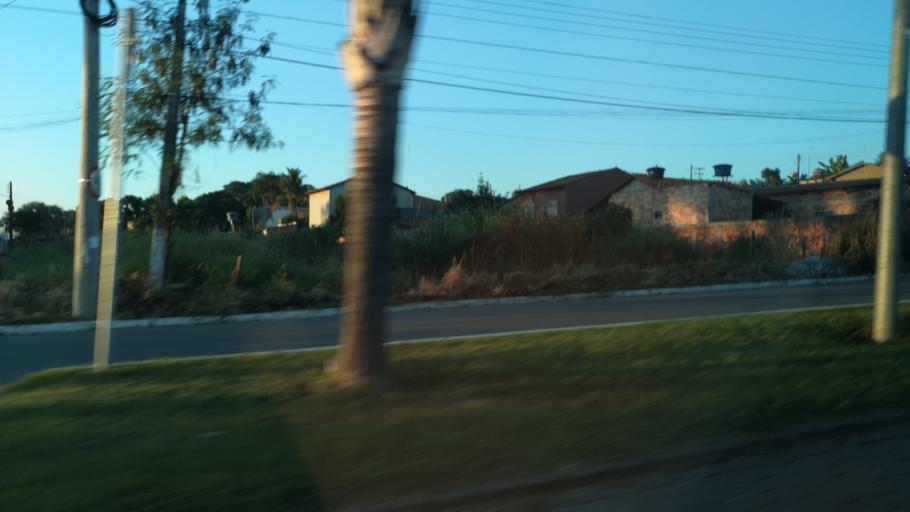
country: BR
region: Goias
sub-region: Senador Canedo
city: Senador Canedo
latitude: -16.6905
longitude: -49.0946
